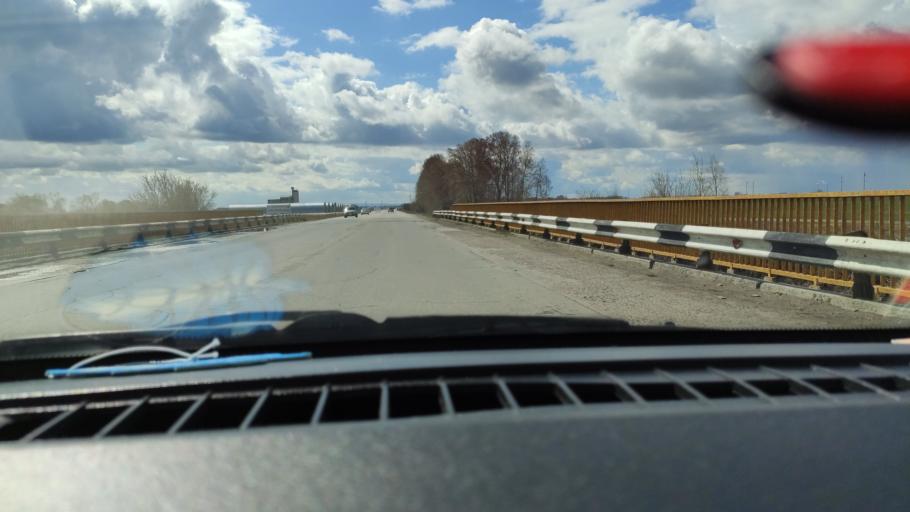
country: RU
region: Samara
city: Tol'yatti
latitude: 53.6899
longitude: 49.4181
